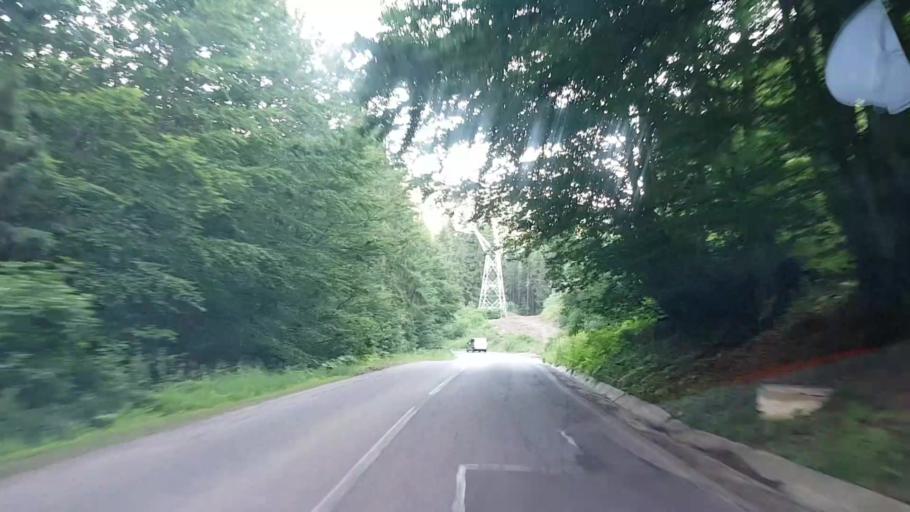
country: RO
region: Harghita
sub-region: Comuna Praid
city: Ocna de Sus
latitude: 46.5854
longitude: 25.2435
